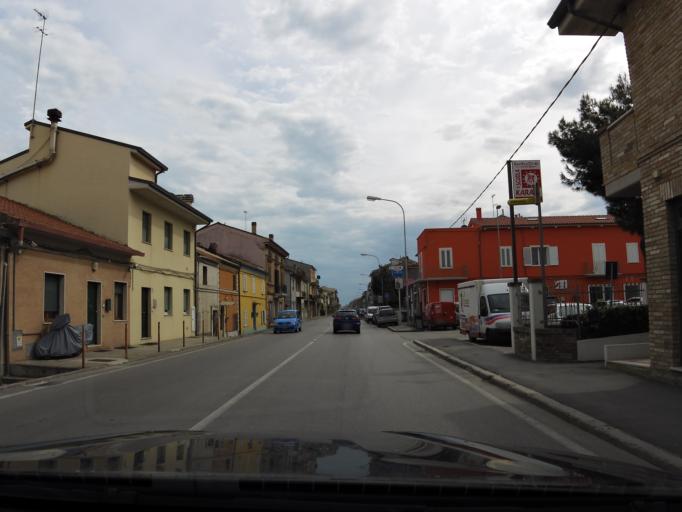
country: IT
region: The Marches
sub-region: Provincia di Macerata
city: Civitanova Marche
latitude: 43.3285
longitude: 13.7140
